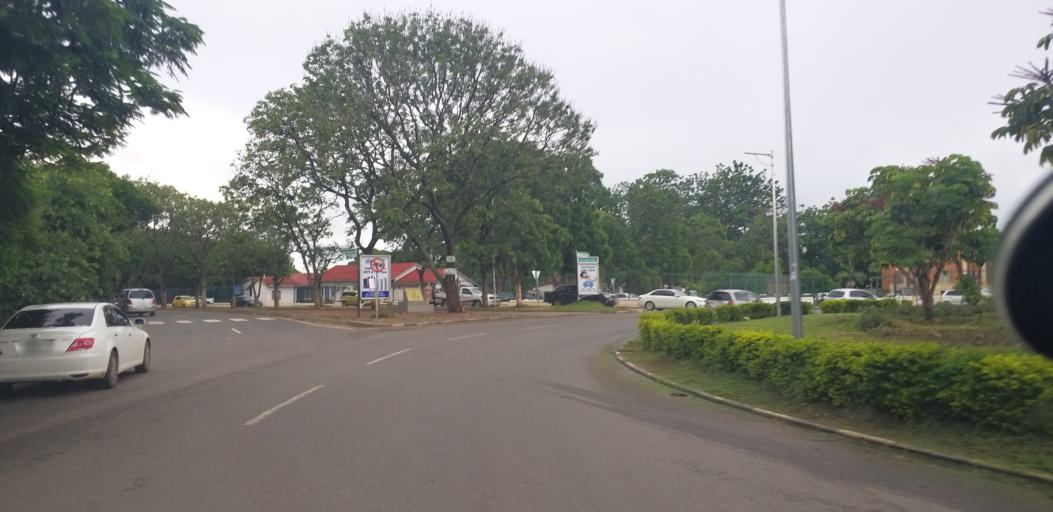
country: ZM
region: Lusaka
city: Lusaka
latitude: -15.4192
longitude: 28.3043
